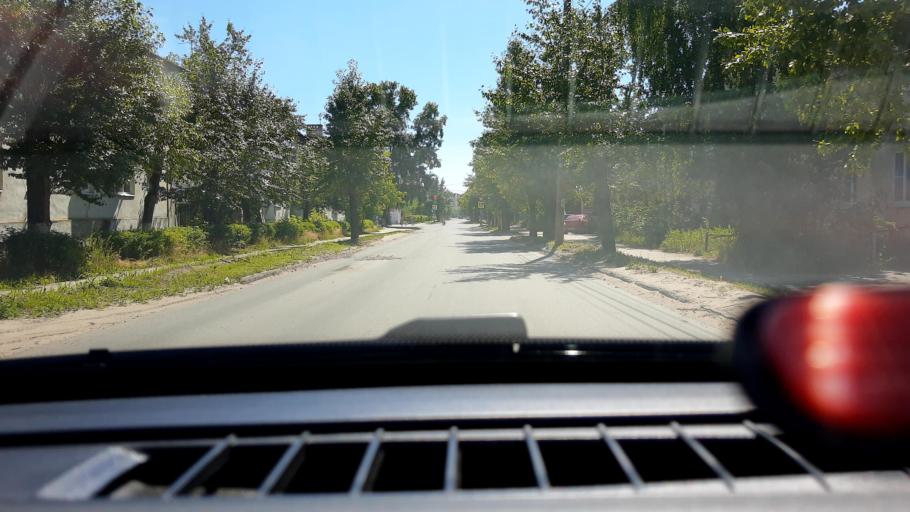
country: RU
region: Nizjnij Novgorod
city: Dzerzhinsk
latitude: 56.2487
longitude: 43.4729
